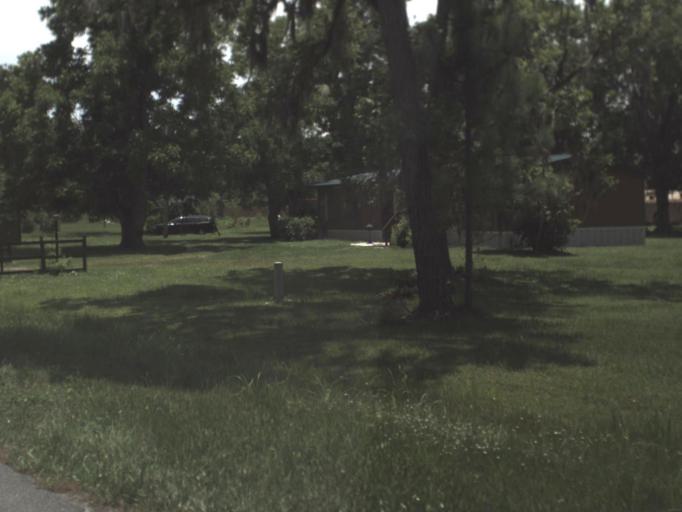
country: US
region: Florida
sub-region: Bradford County
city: Starke
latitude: 30.0009
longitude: -82.1346
